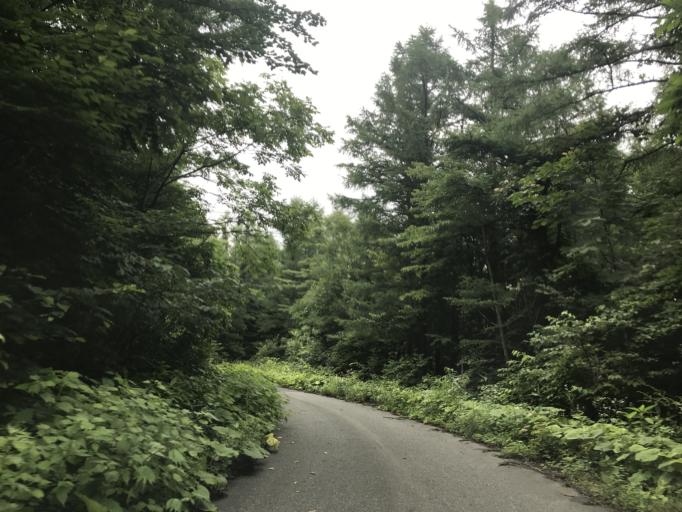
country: JP
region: Iwate
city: Ichinoseki
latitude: 38.9378
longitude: 140.8773
